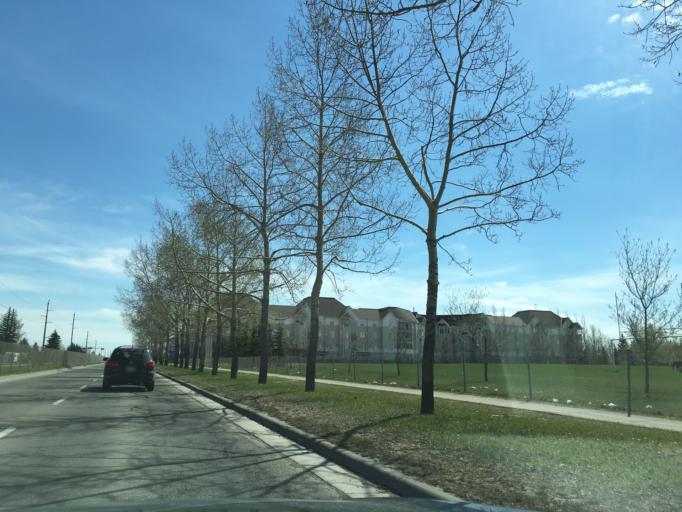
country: CA
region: Alberta
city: Calgary
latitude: 50.9065
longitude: -114.0518
